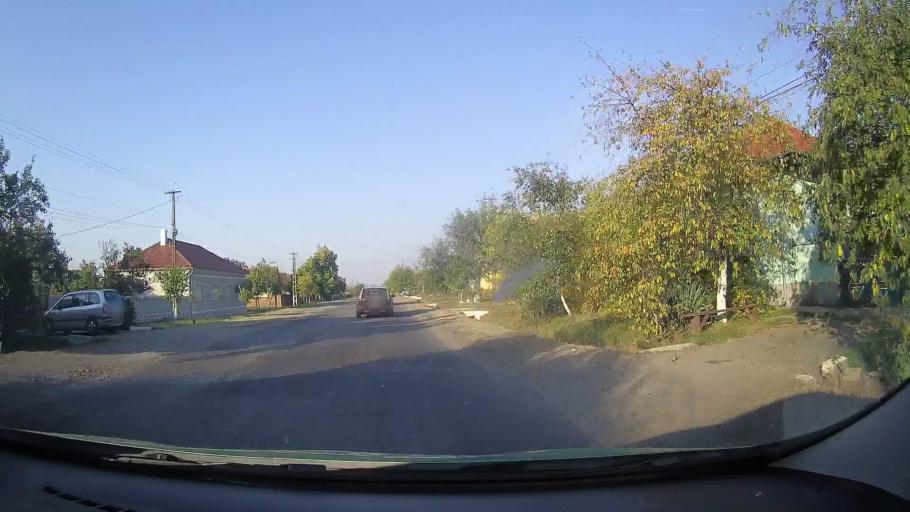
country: RO
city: Masca
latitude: 46.2974
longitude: 21.6711
